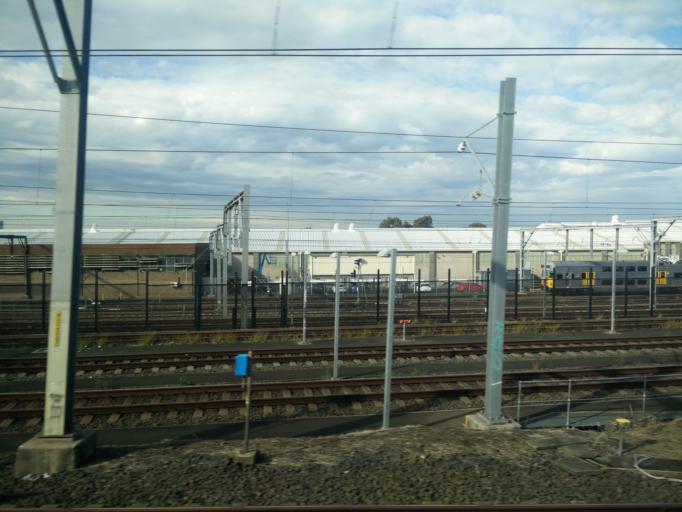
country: AU
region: New South Wales
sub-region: City of Sydney
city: Darlington
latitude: -33.8958
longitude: 151.1891
